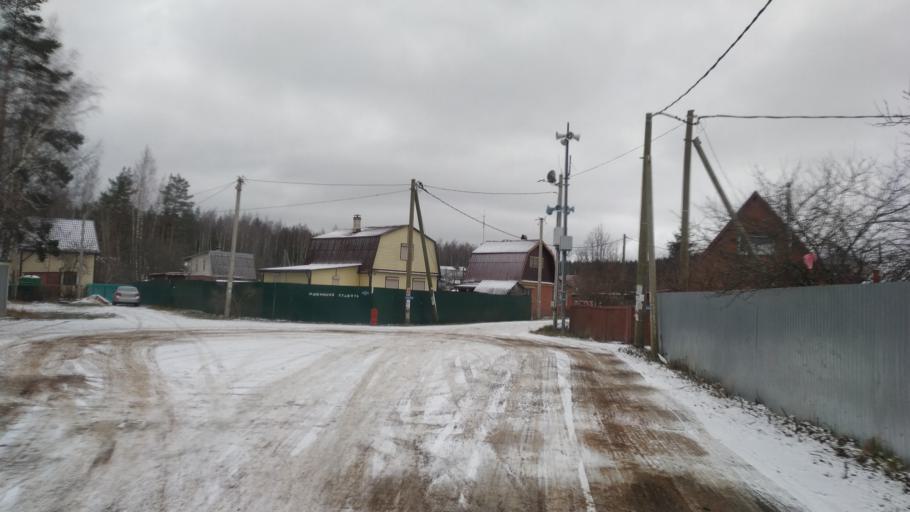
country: RU
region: Leningrad
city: Sosnovyy Bor
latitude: 59.8551
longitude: 29.1034
